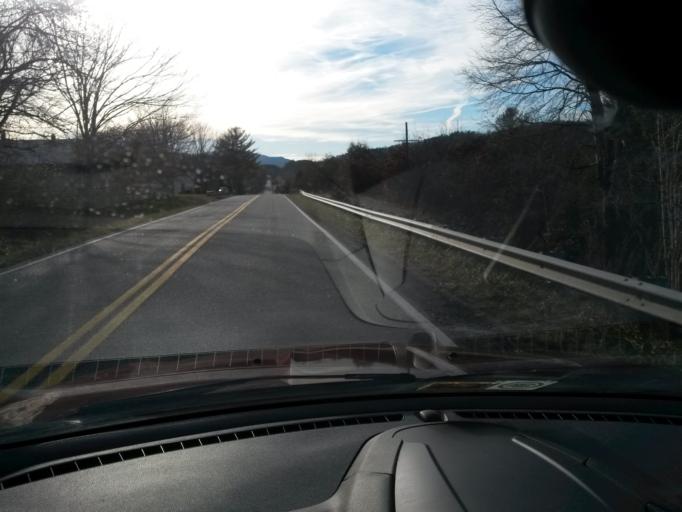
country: US
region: Virginia
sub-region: Alleghany County
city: Clifton Forge
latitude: 37.8484
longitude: -79.7430
